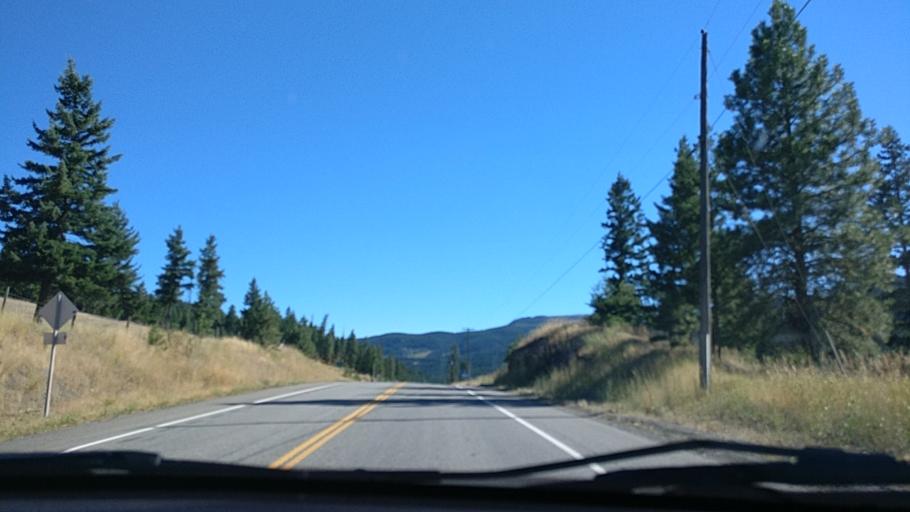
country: CA
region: British Columbia
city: Chase
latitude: 50.5820
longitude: -119.8877
